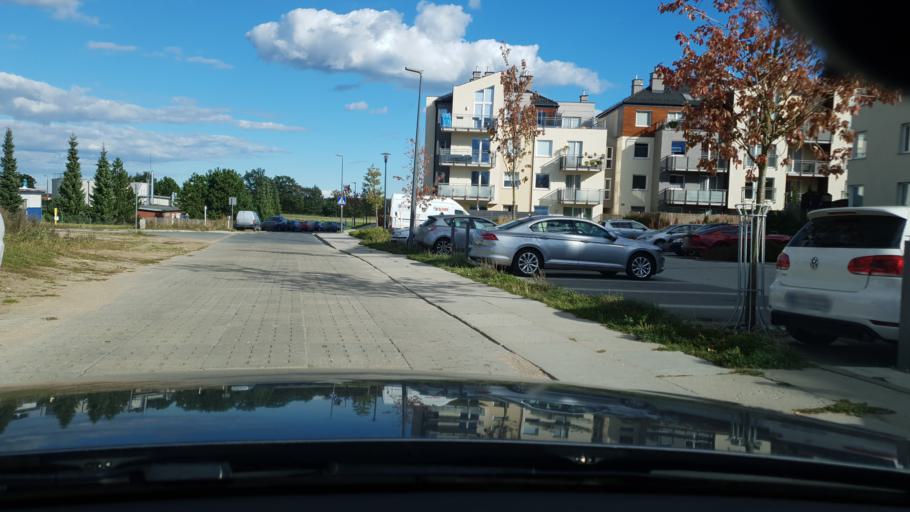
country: PL
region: Pomeranian Voivodeship
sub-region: Powiat kartuski
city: Chwaszczyno
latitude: 54.4948
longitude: 18.4389
